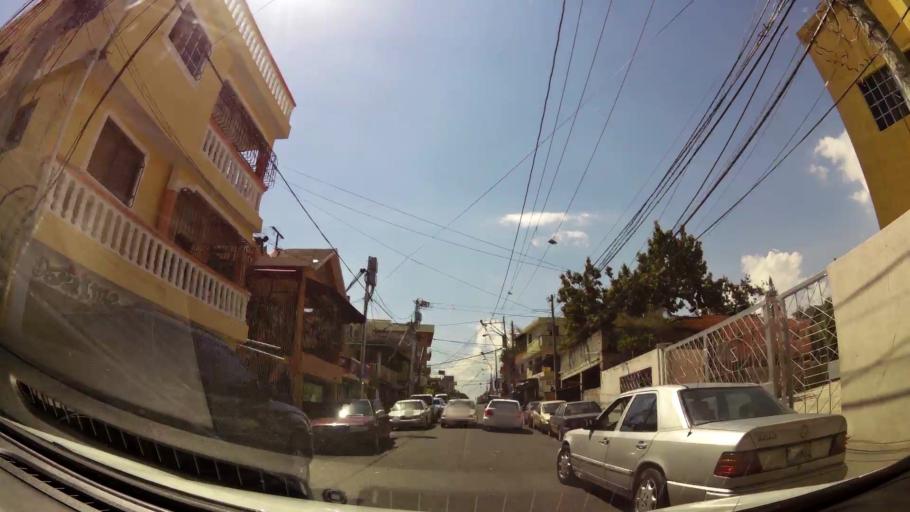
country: DO
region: Nacional
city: Bella Vista
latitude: 18.4645
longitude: -69.9760
